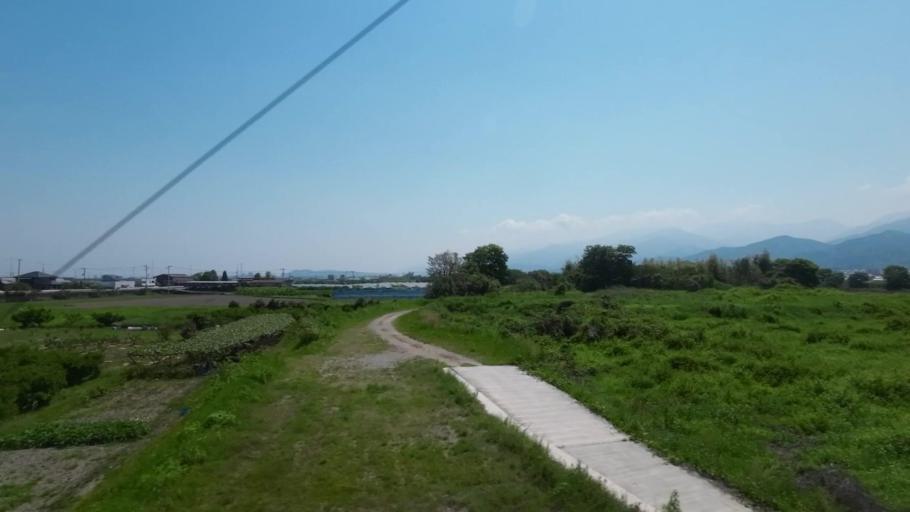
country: JP
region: Ehime
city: Saijo
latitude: 33.9073
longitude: 133.0993
